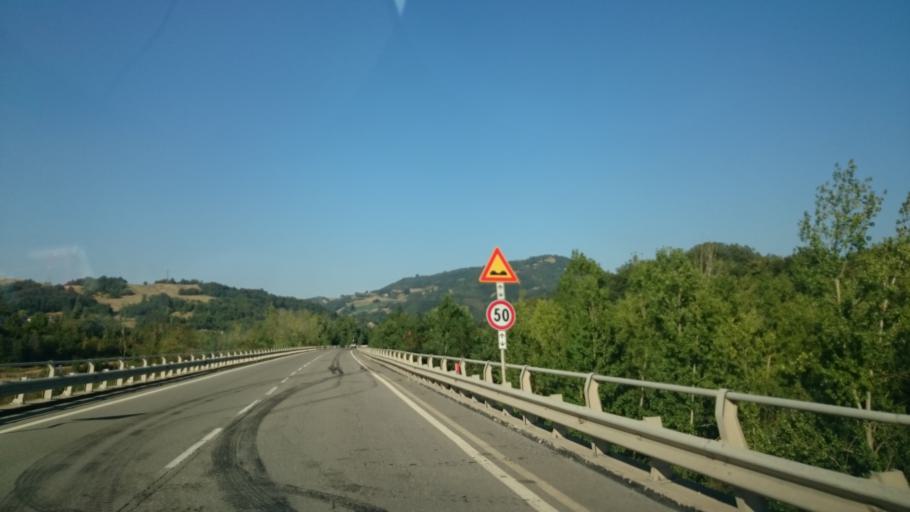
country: IT
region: Emilia-Romagna
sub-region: Provincia di Modena
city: Prignano
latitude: 44.4241
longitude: 10.6355
